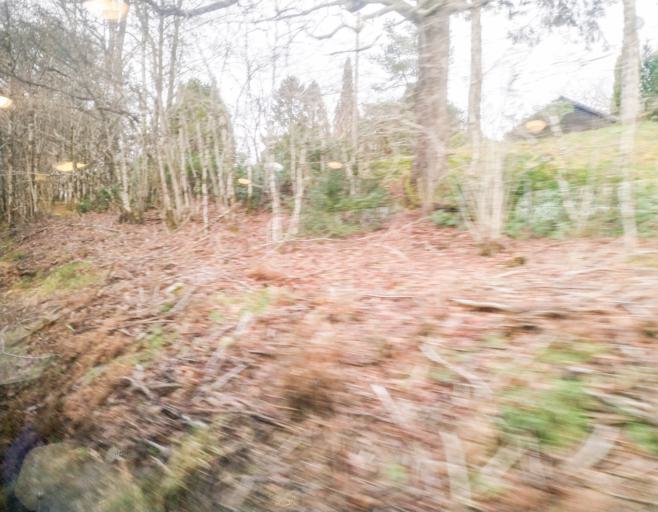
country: GB
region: Scotland
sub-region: Highland
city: Spean Bridge
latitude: 56.8927
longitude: -4.8869
